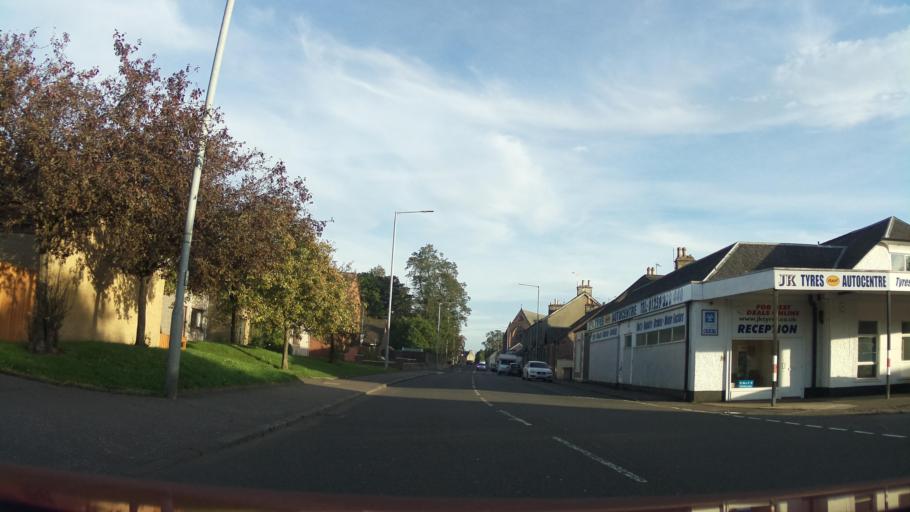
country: GB
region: Scotland
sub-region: Clackmannanshire
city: Alloa
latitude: 56.1204
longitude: -3.7989
